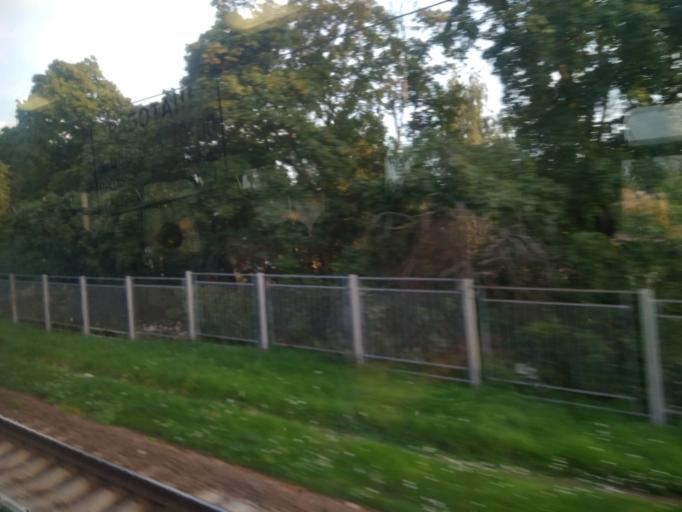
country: RU
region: Moskovskaya
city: Malakhovka
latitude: 55.6434
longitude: 38.0140
